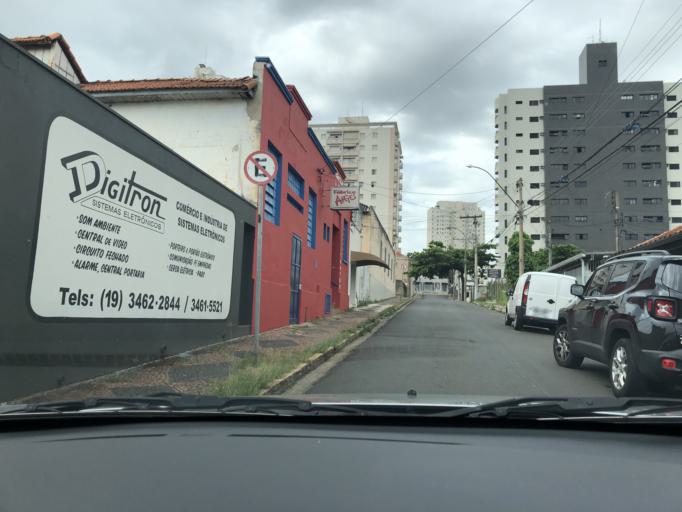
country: BR
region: Sao Paulo
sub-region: Americana
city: Americana
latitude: -22.7375
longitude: -47.3351
